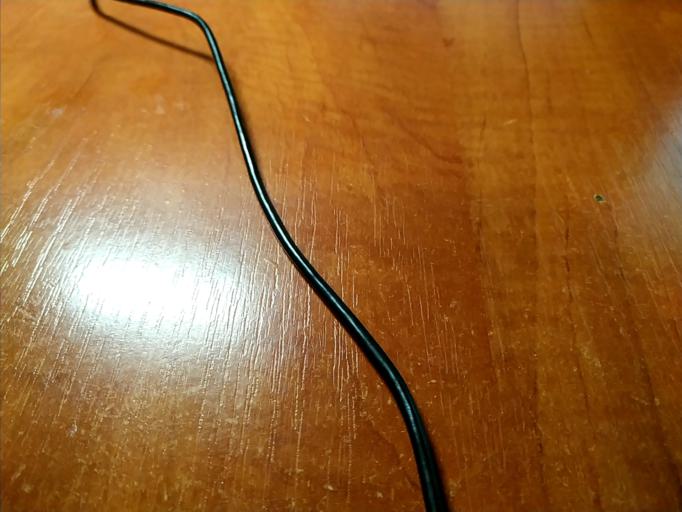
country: RU
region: Tverskaya
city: Ves'yegonsk
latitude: 58.8016
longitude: 37.5436
